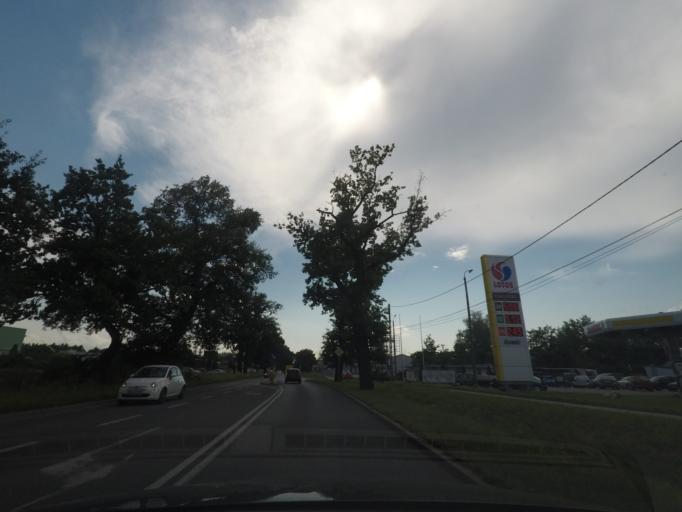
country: PL
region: Lesser Poland Voivodeship
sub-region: Powiat oswiecimski
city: Przecieszyn
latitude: 49.9909
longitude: 19.1657
